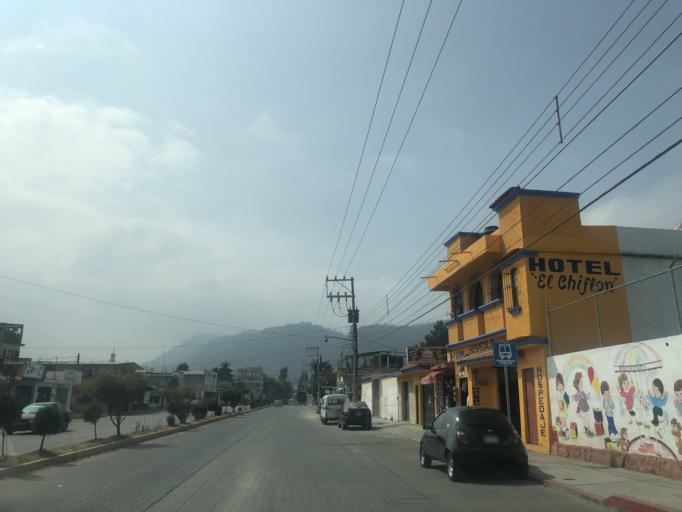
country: MX
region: Chiapas
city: San Cristobal de las Casas
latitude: 16.7156
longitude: -92.6356
